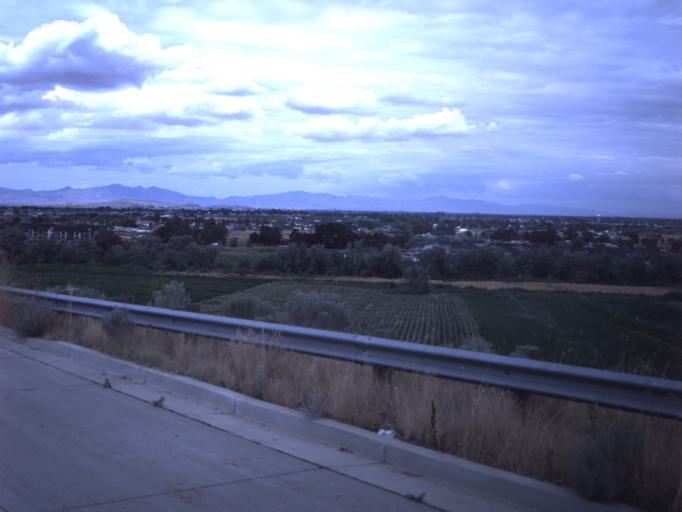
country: US
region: Utah
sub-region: Weber County
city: West Haven
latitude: 41.1980
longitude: -112.0279
